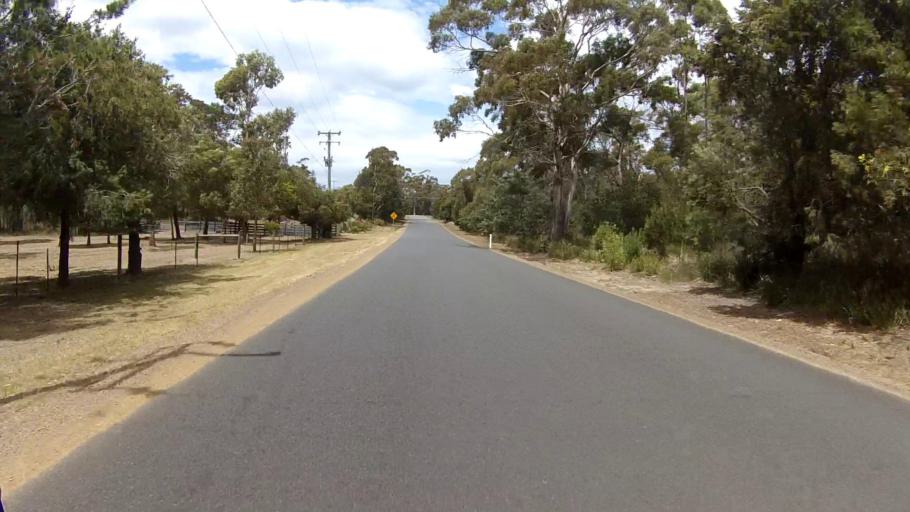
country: AU
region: Tasmania
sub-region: Sorell
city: Sorell
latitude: -42.5755
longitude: 147.9010
